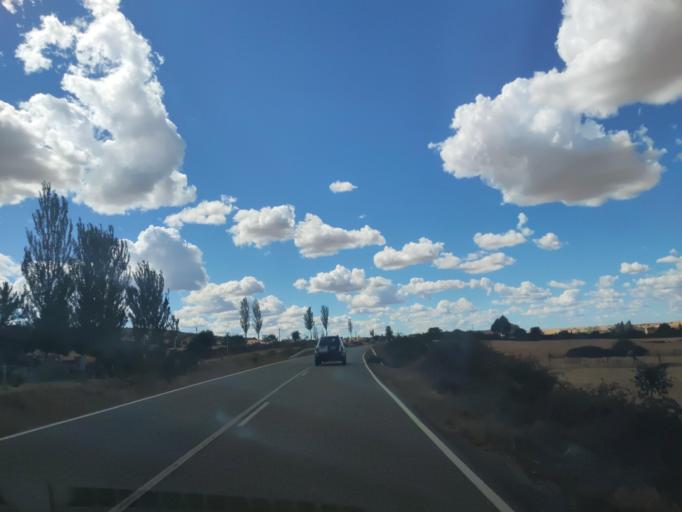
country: ES
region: Castille and Leon
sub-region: Provincia de Salamanca
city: Tamames
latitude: 40.6531
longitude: -6.0961
